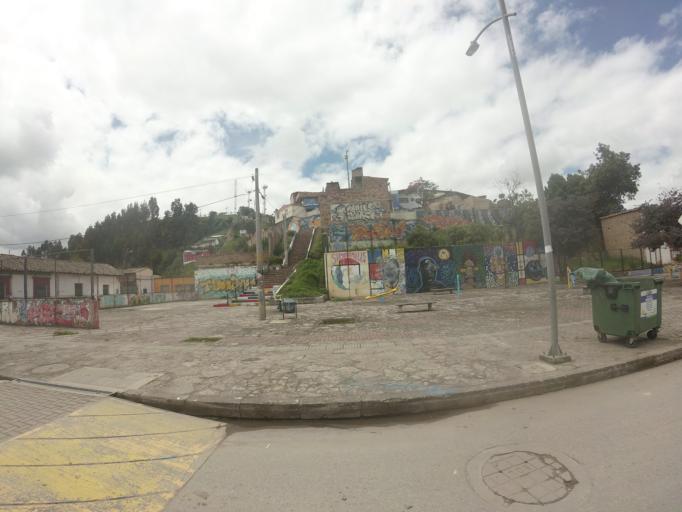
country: CO
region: Boyaca
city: Duitama
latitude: 5.8234
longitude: -73.0320
